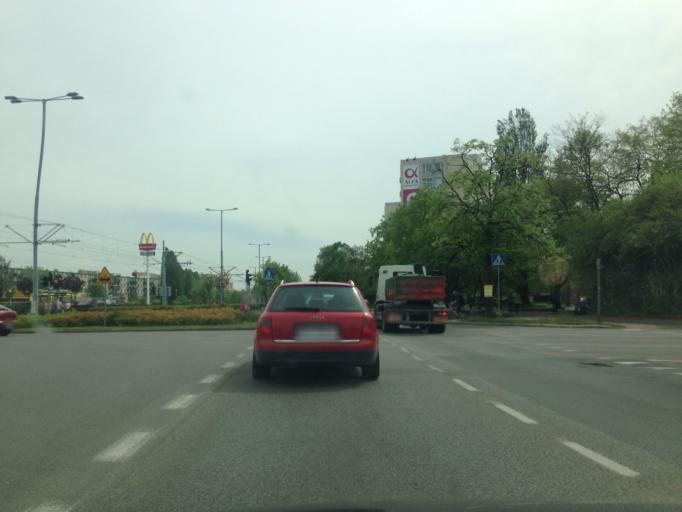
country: PL
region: Pomeranian Voivodeship
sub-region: Sopot
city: Sopot
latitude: 54.4085
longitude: 18.5886
